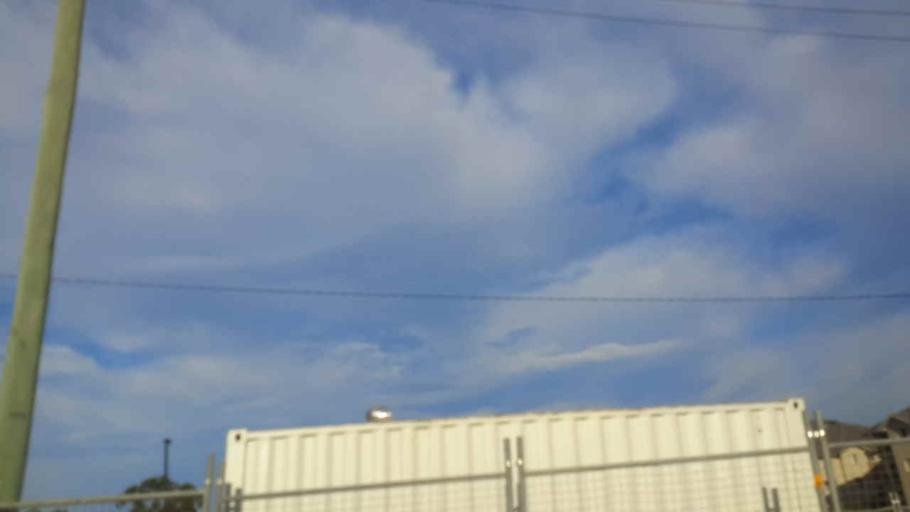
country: AU
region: New South Wales
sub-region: Campbelltown Municipality
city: Campbelltown
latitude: -34.0757
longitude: 150.8081
